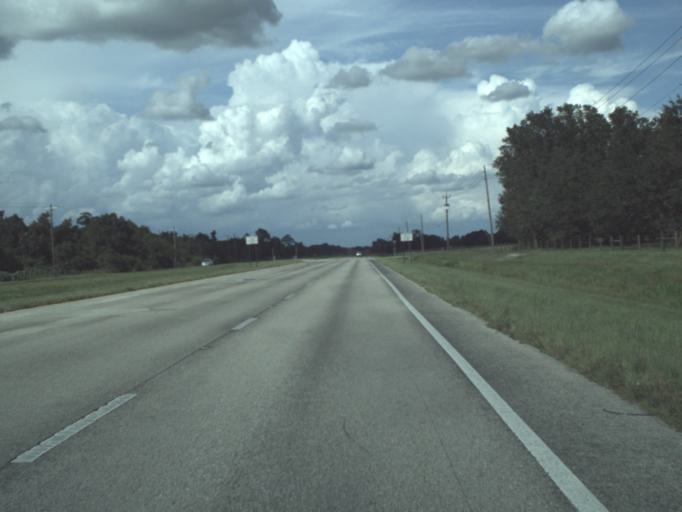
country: US
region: Florida
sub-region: DeSoto County
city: Arcadia
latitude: 27.3205
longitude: -81.8142
